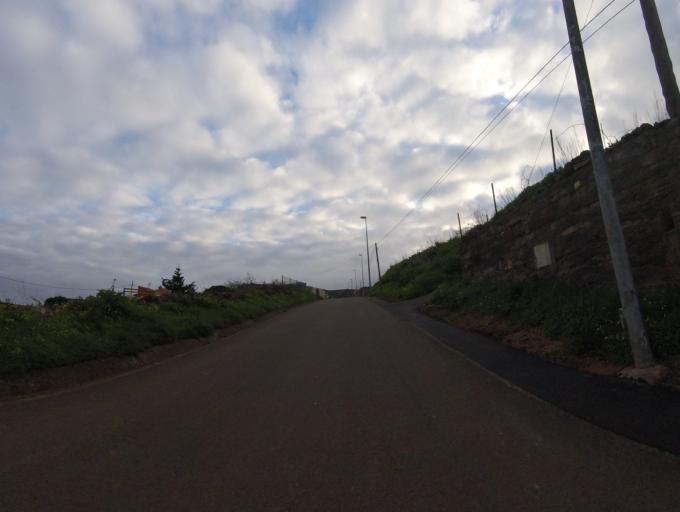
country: ES
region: Canary Islands
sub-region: Provincia de Santa Cruz de Tenerife
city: La Laguna
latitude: 28.4515
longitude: -16.3527
